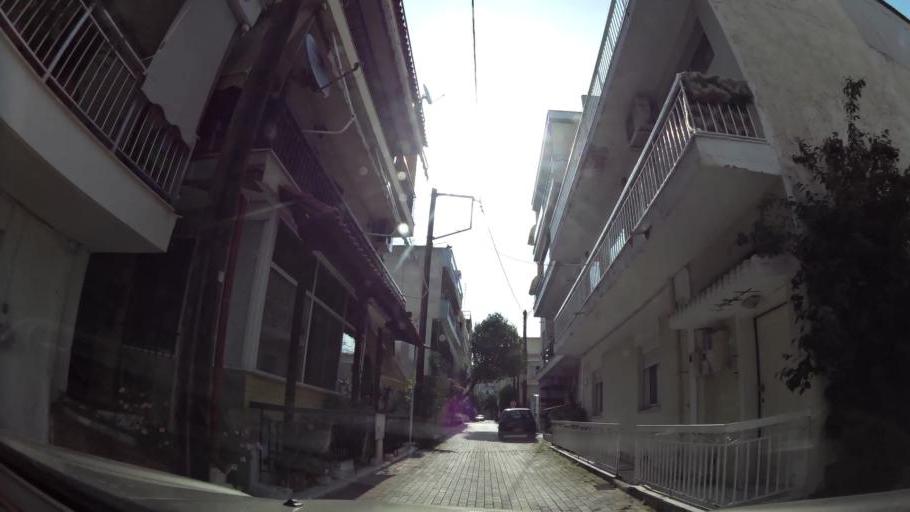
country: GR
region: Central Macedonia
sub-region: Nomos Thessalonikis
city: Evosmos
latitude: 40.6641
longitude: 22.9178
